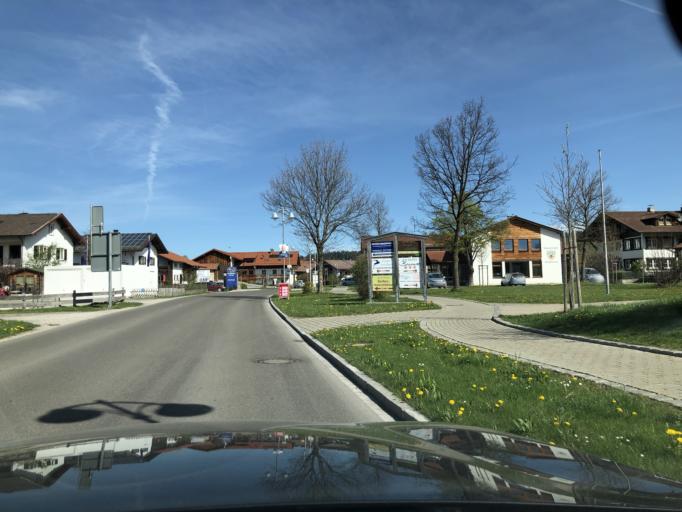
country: DE
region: Bavaria
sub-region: Swabia
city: Hopferau
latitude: 47.6095
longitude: 10.6380
